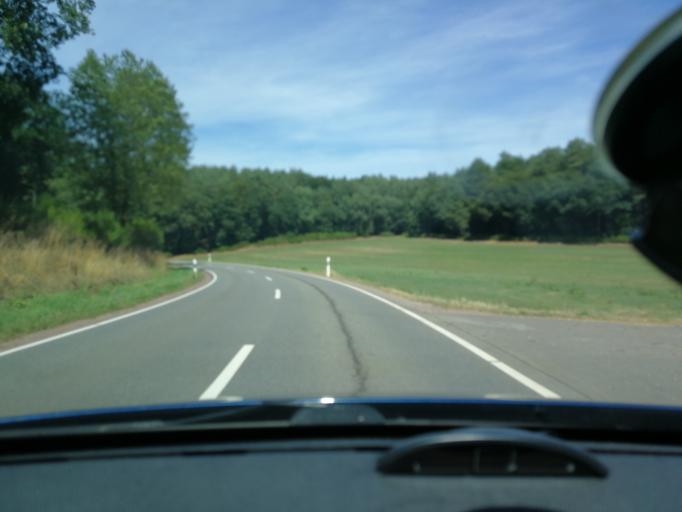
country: DE
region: Rheinland-Pfalz
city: Heidweiler
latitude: 49.9201
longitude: 6.7556
